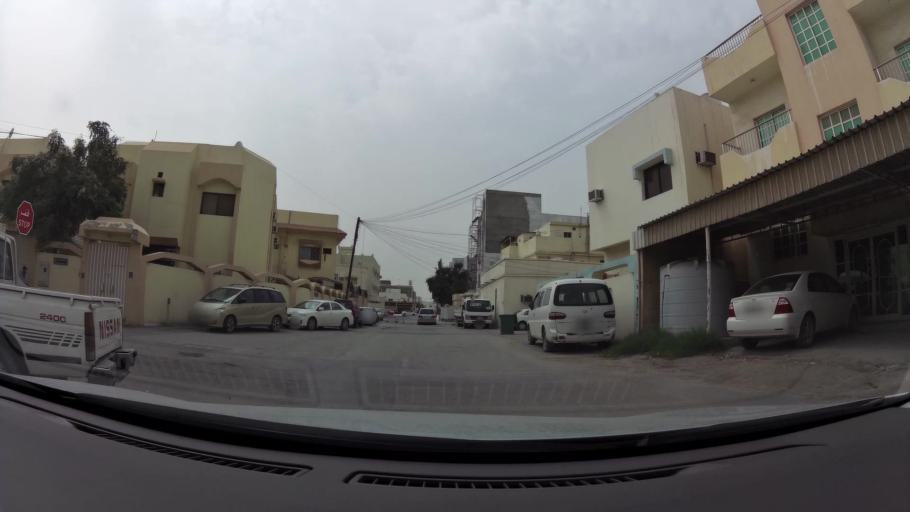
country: QA
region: Baladiyat ad Dawhah
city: Doha
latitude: 25.2536
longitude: 51.5549
